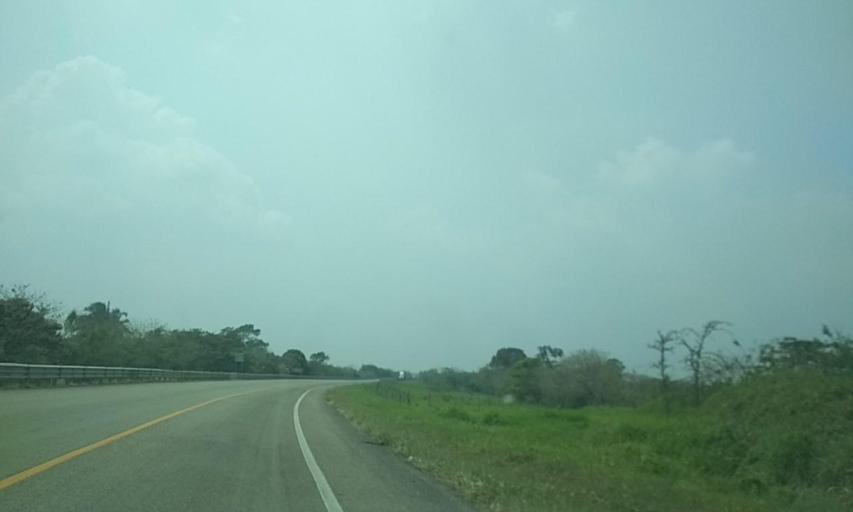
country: MX
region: Tabasco
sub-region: Huimanguillo
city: Francisco Rueda
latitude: 17.7731
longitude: -94.0461
